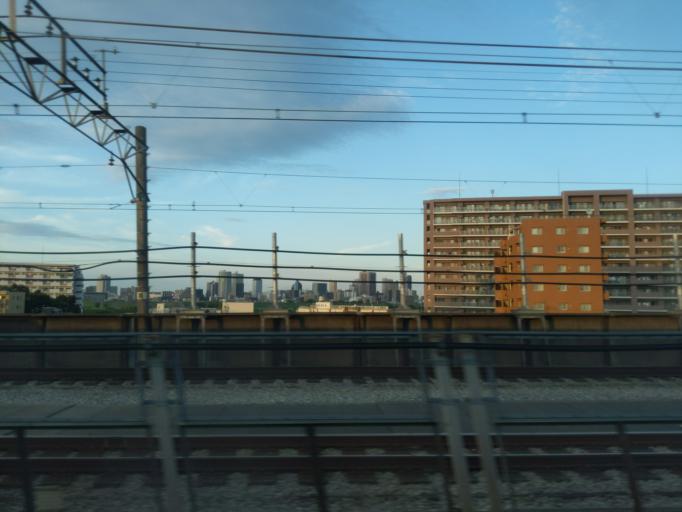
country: JP
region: Saitama
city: Kawaguchi
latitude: 35.7885
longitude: 139.7035
